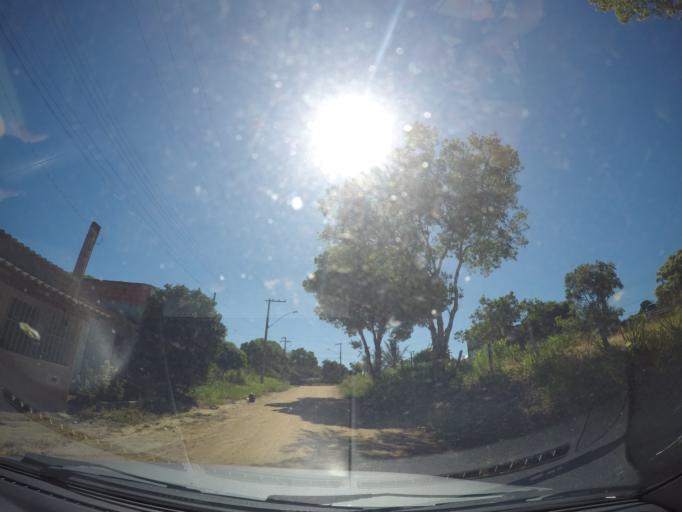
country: BR
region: Espirito Santo
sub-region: Aracruz
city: Aracruz
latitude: -19.9215
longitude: -40.1196
